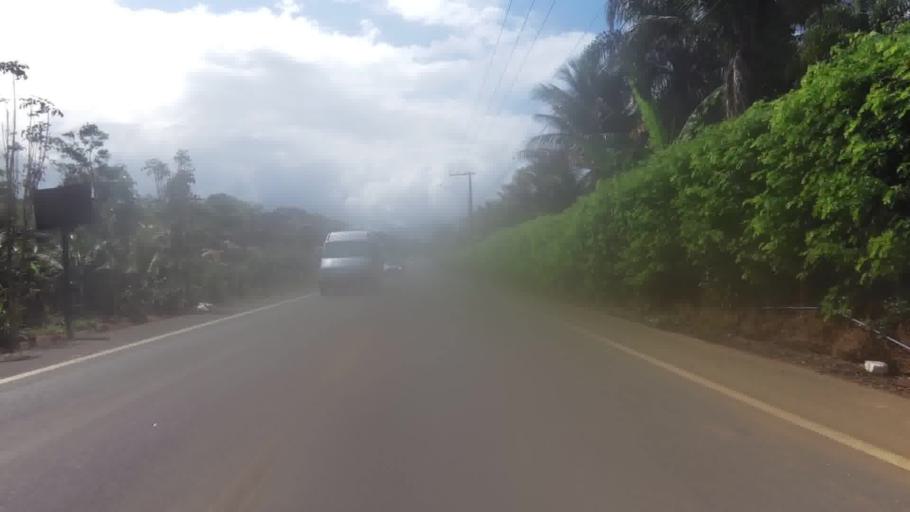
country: BR
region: Espirito Santo
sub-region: Piuma
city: Piuma
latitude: -20.8112
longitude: -40.6829
